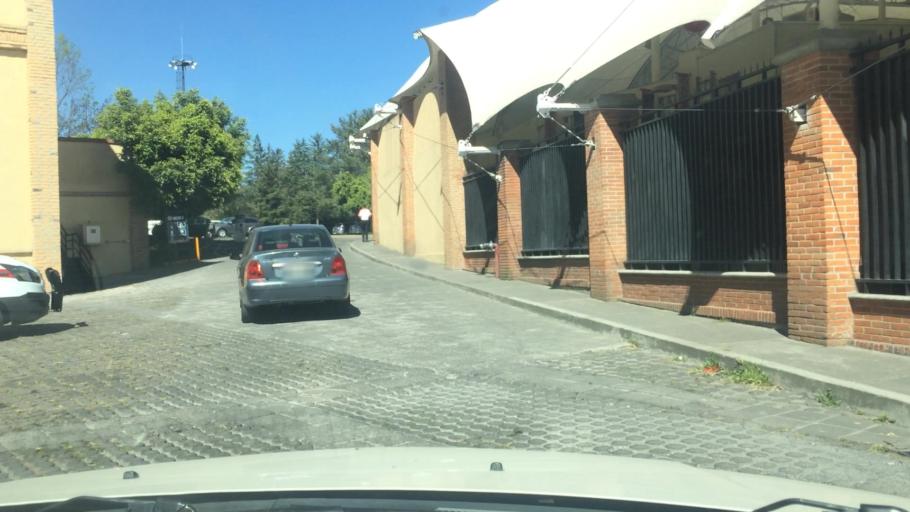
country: MX
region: Mexico City
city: Tlalpan
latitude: 19.2982
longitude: -99.1803
